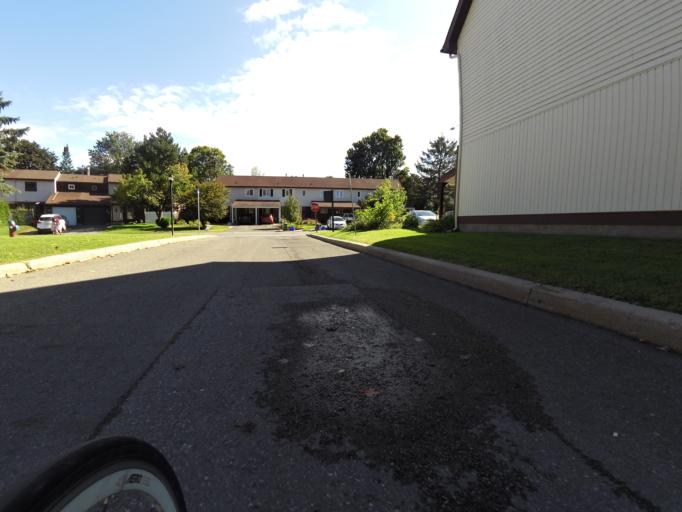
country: CA
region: Ontario
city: Bells Corners
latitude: 45.3171
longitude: -75.8337
